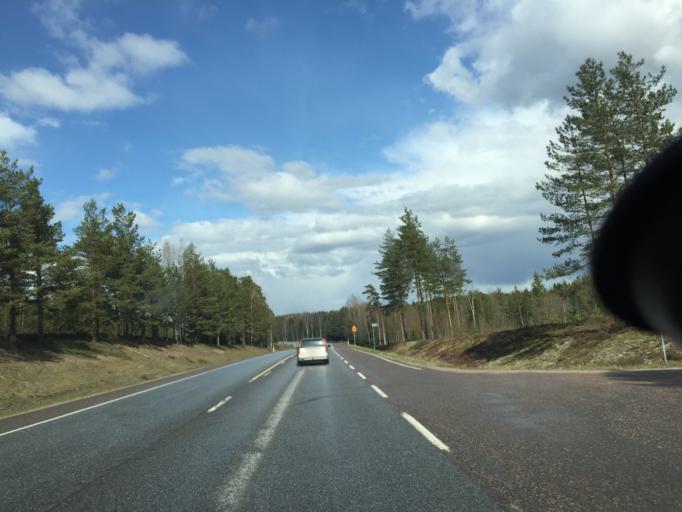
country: FI
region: Uusimaa
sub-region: Raaseporin
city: Karis
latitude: 60.0841
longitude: 23.7348
